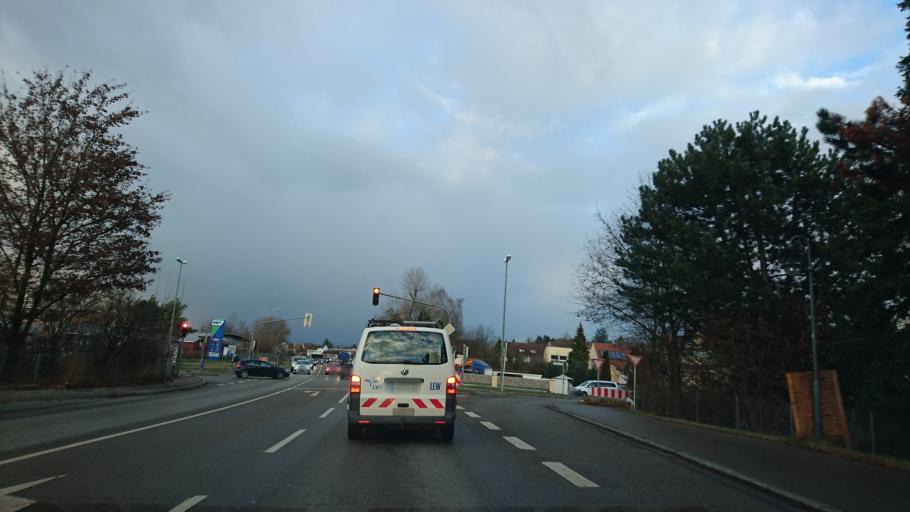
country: DE
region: Bavaria
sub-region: Swabia
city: Diedorf
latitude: 48.3623
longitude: 10.7898
